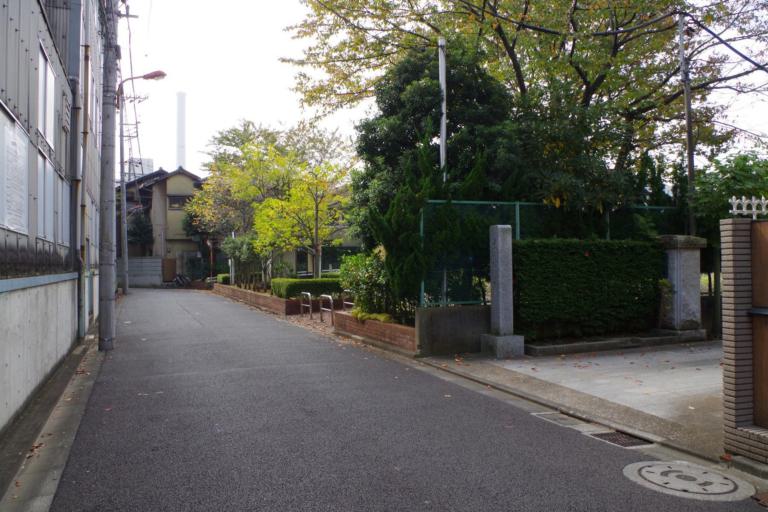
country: JP
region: Tokyo
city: Urayasu
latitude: 35.7210
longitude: 139.8361
